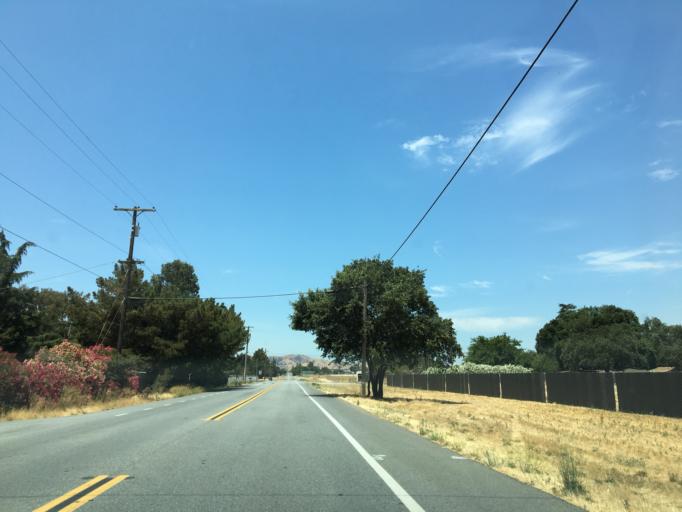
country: US
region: California
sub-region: Santa Clara County
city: Morgan Hill
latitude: 37.1548
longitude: -121.6884
